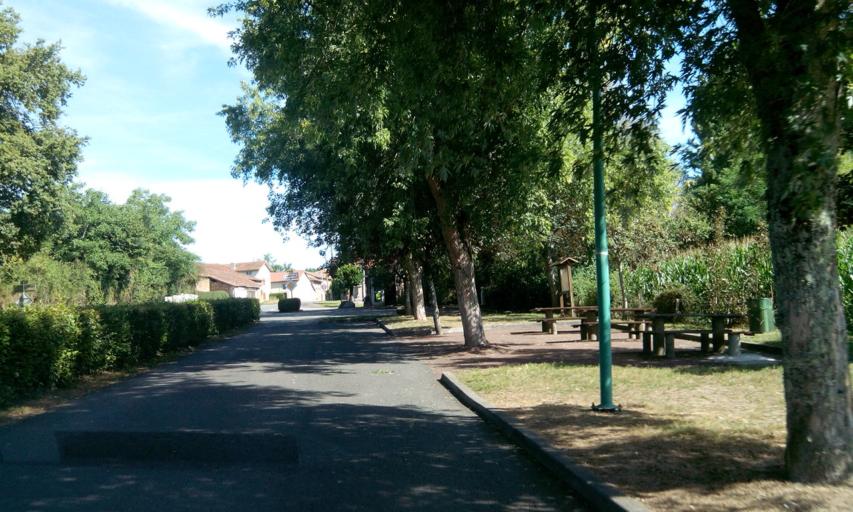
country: FR
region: Poitou-Charentes
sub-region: Departement de la Charente
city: Etagnac
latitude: 45.9302
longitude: 0.7387
